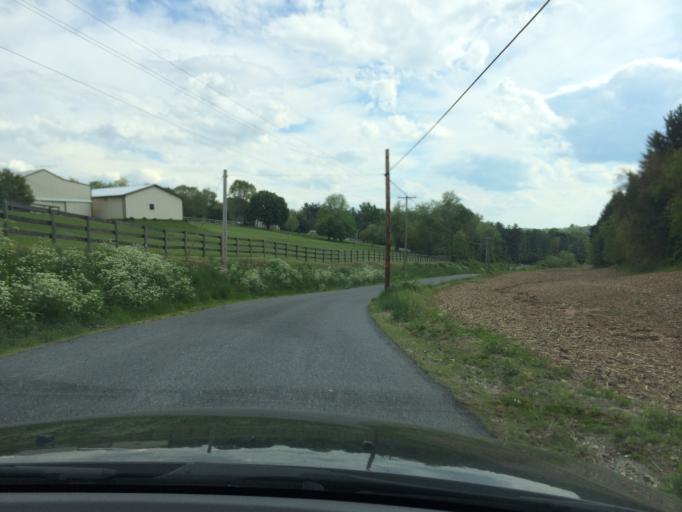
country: US
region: Maryland
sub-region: Carroll County
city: Westminster
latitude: 39.4929
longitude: -76.9986
